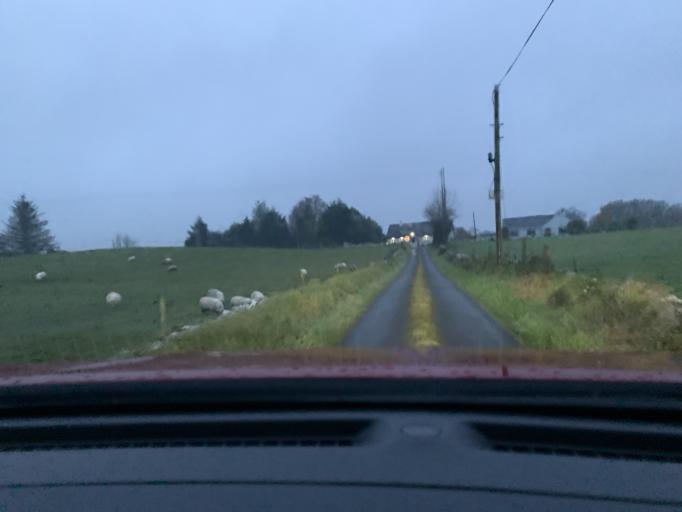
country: IE
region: Connaught
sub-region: Sligo
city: Ballymote
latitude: 54.0208
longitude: -8.5619
